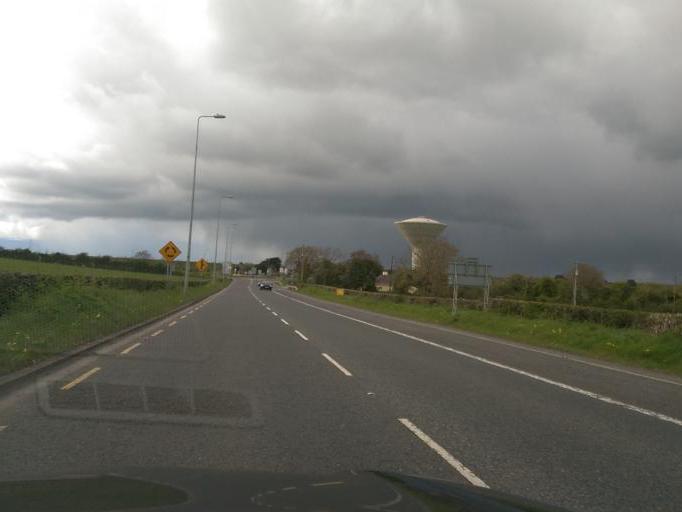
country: IE
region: Leinster
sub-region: An Mhi
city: Dunshaughlin
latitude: 53.5200
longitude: -6.5489
